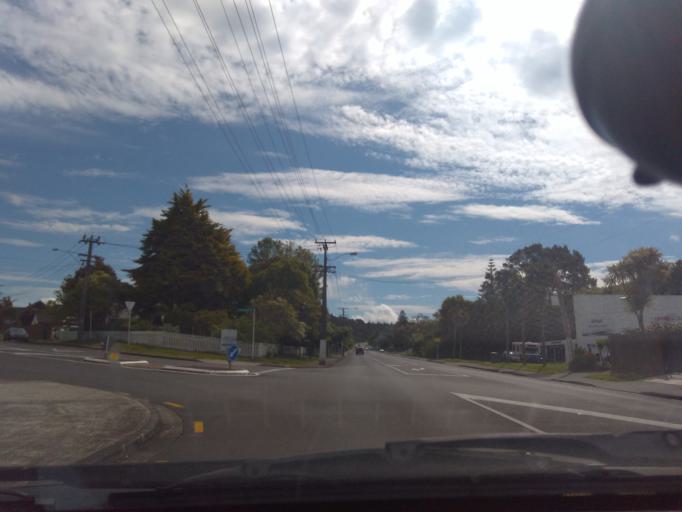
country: NZ
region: Auckland
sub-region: Auckland
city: Titirangi
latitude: -36.9314
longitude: 174.6753
